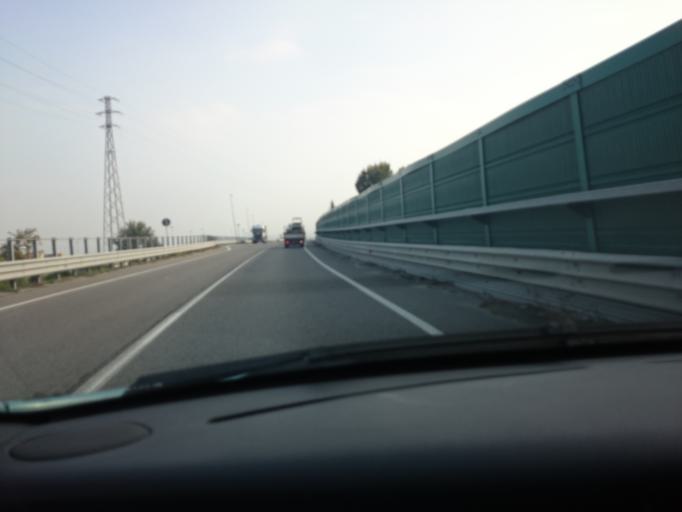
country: IT
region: Emilia-Romagna
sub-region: Provincia di Reggio Emilia
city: Veggia-Villalunga
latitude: 44.5739
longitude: 10.7486
